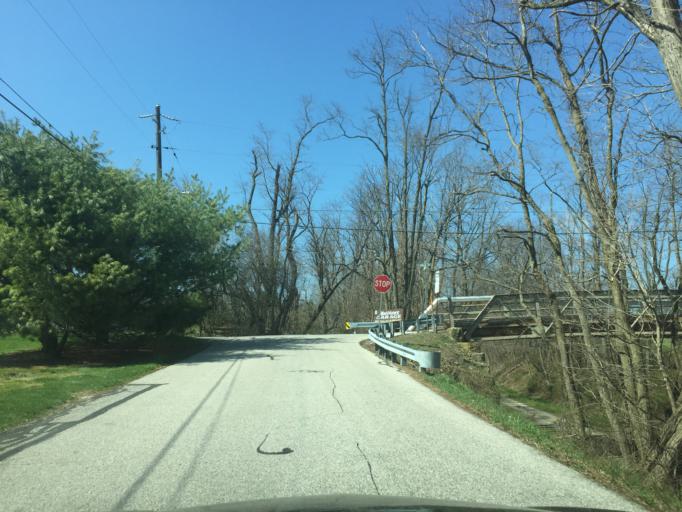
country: US
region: Pennsylvania
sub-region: York County
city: New Freedom
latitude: 39.7270
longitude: -76.7027
